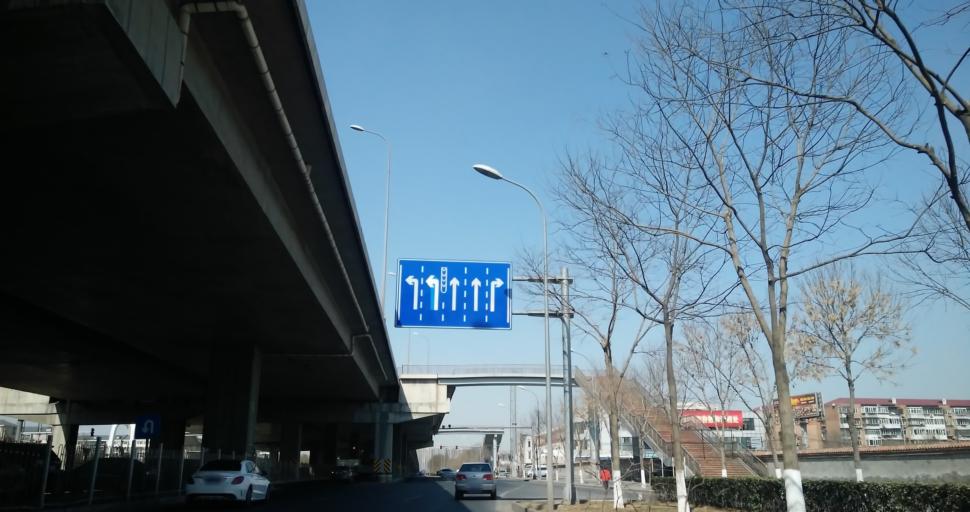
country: CN
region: Beijing
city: Jiugong
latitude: 39.8011
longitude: 116.4238
